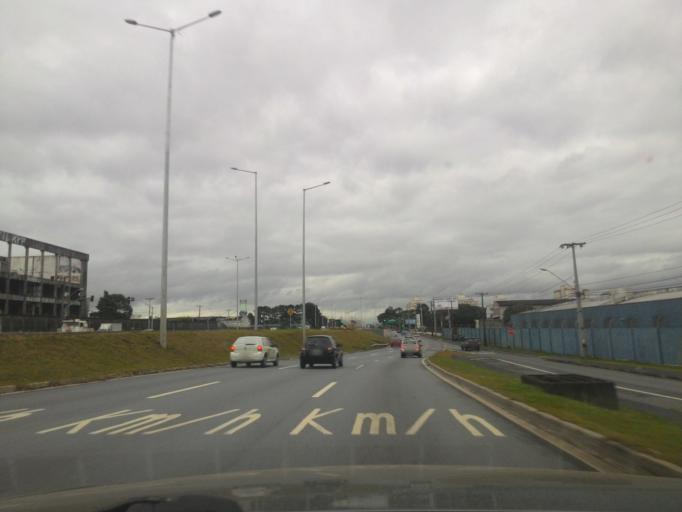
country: BR
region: Parana
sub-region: Sao Jose Dos Pinhais
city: Sao Jose dos Pinhais
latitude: -25.5197
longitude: -49.2932
